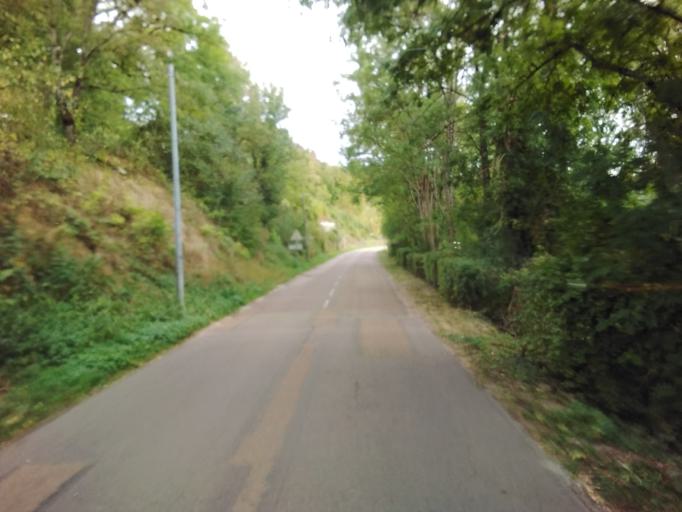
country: FR
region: Champagne-Ardenne
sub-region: Departement de l'Aube
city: Les Riceys
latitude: 47.9349
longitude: 4.3551
